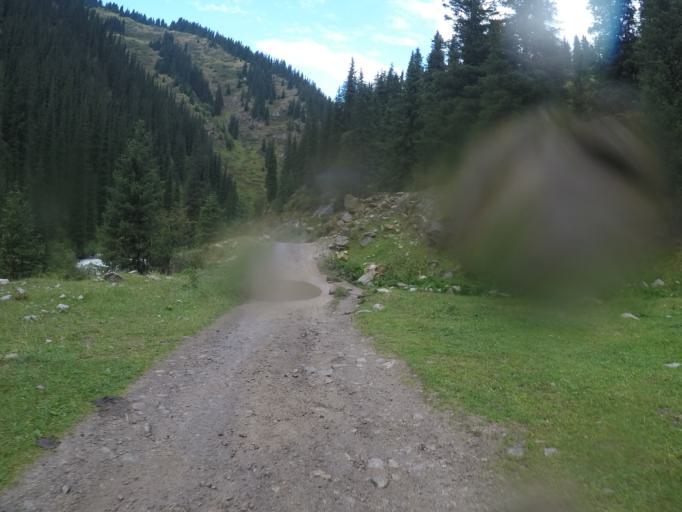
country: KG
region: Ysyk-Koel
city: Teploklyuchenka
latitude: 42.4135
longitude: 78.5734
